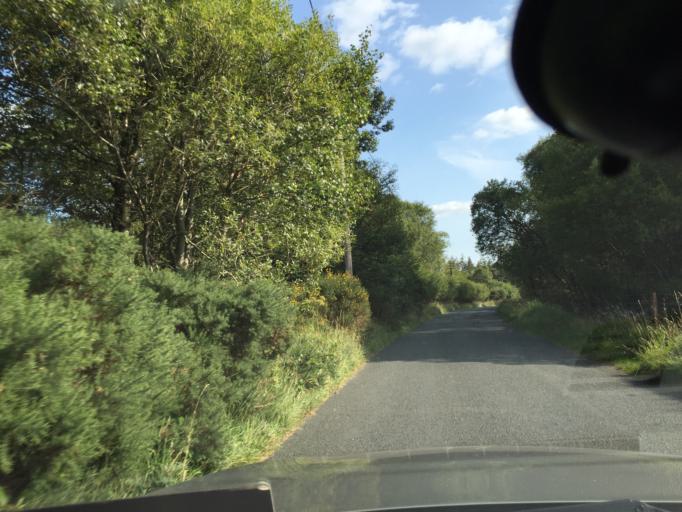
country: IE
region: Leinster
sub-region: Wicklow
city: Rathdrum
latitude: 53.0190
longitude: -6.3034
